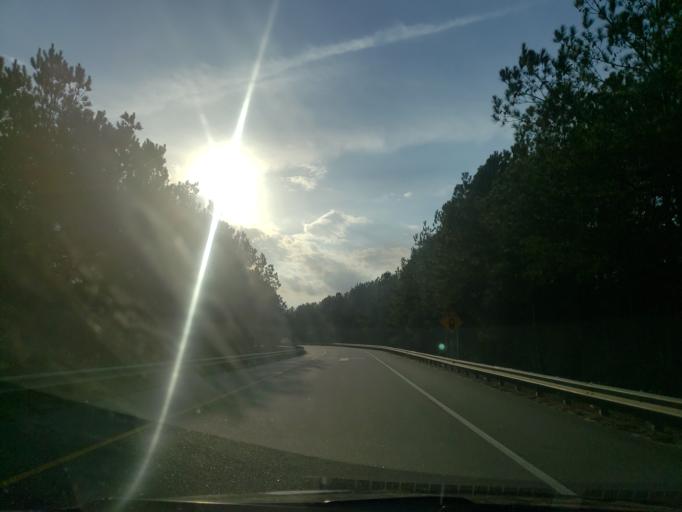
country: US
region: Georgia
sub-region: Chatham County
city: Port Wentworth
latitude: 32.1695
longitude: -81.2151
